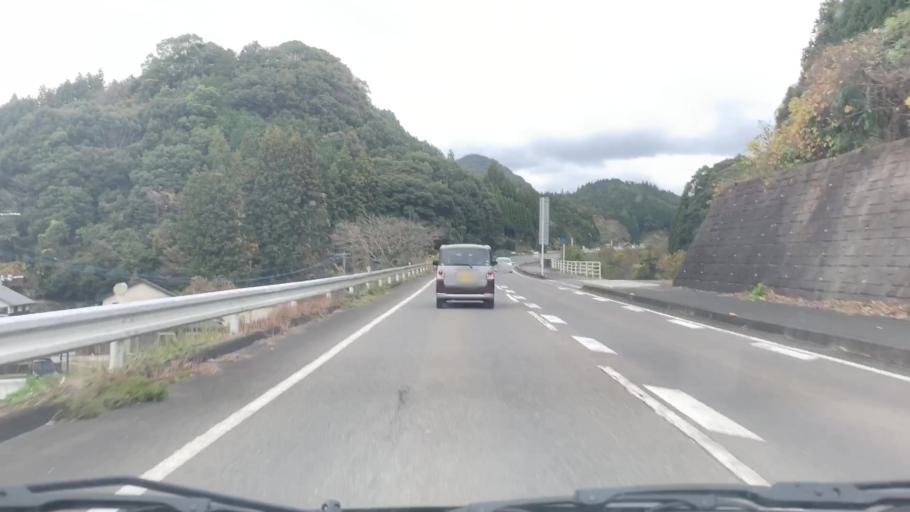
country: JP
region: Saga Prefecture
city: Ureshinomachi-shimojuku
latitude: 33.0931
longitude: 130.0282
